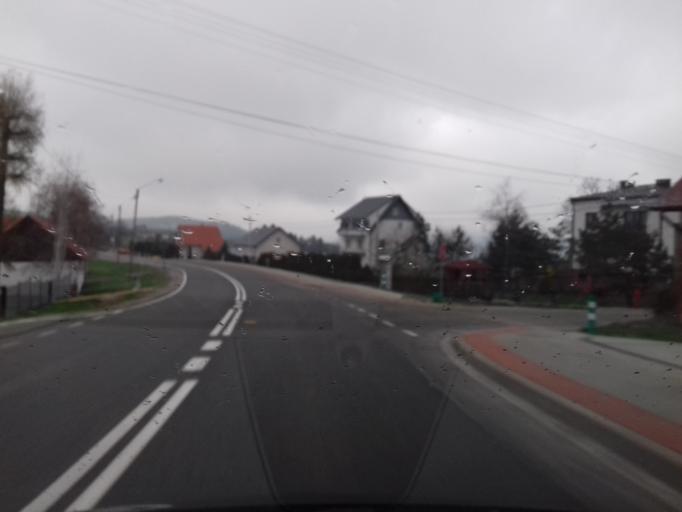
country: PL
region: Lesser Poland Voivodeship
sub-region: Powiat limanowski
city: Lukowica
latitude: 49.6657
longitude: 20.5066
